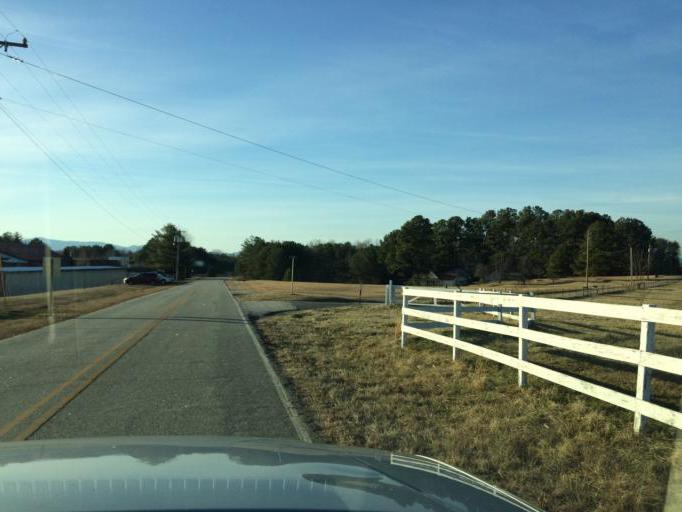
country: US
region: South Carolina
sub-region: Spartanburg County
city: Landrum
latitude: 35.1487
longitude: -82.1097
